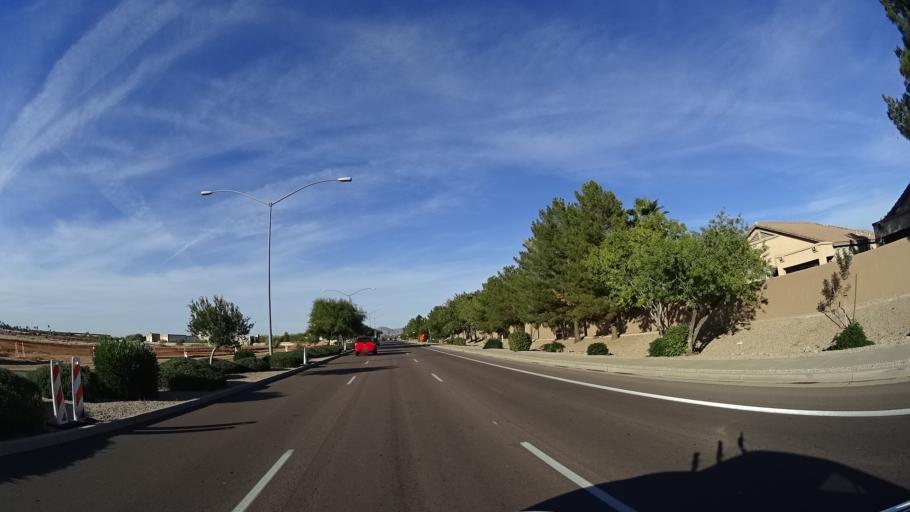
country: US
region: Arizona
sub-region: Pinal County
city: Apache Junction
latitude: 33.3739
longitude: -111.6360
